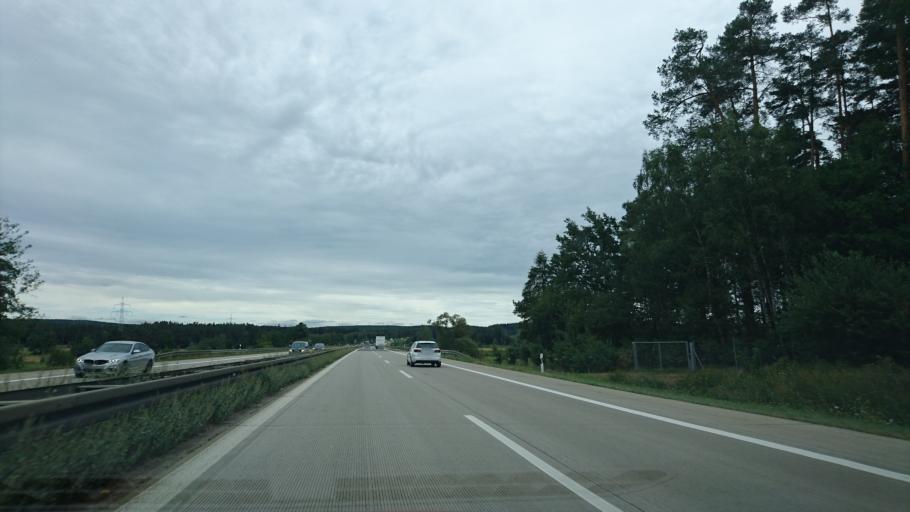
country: DE
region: Bavaria
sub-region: Upper Palatinate
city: Wernberg-Koblitz
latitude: 49.5486
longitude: 12.1271
